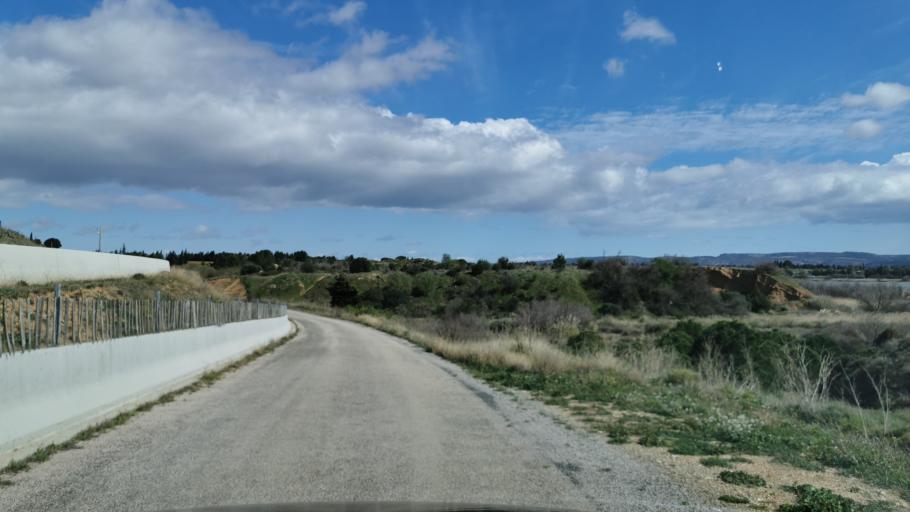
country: FR
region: Languedoc-Roussillon
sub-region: Departement de l'Aude
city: Narbonne
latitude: 43.1507
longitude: 2.9863
